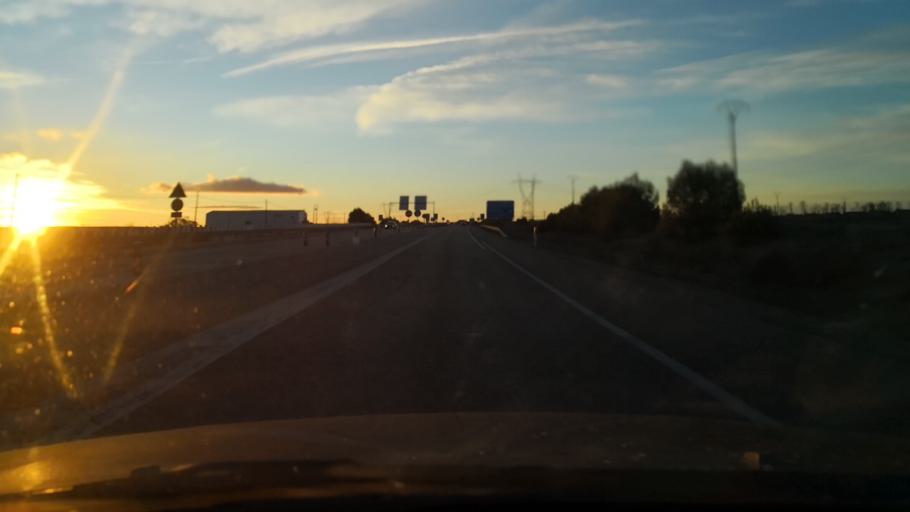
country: ES
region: Castille and Leon
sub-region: Provincia de Valladolid
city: Tordesillas
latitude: 41.5038
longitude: -5.0243
